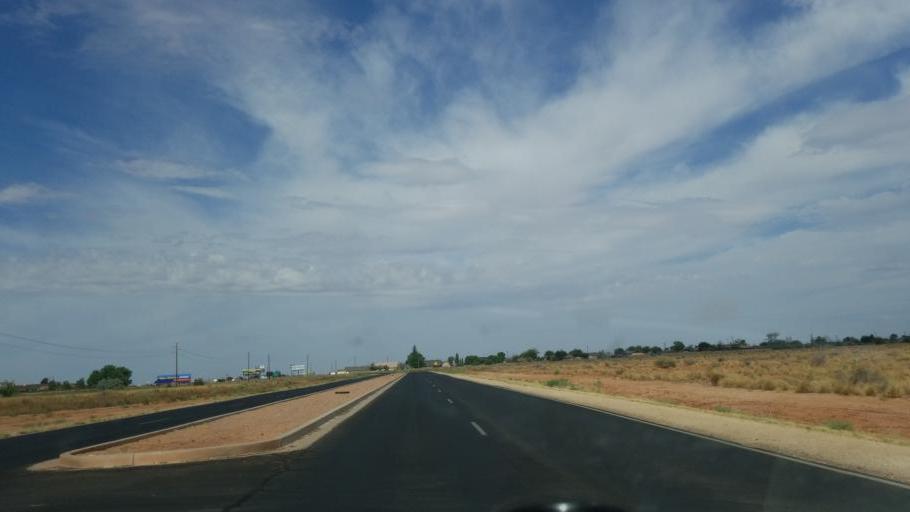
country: US
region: Arizona
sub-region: Navajo County
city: Winslow
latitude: 35.0405
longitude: -110.7113
